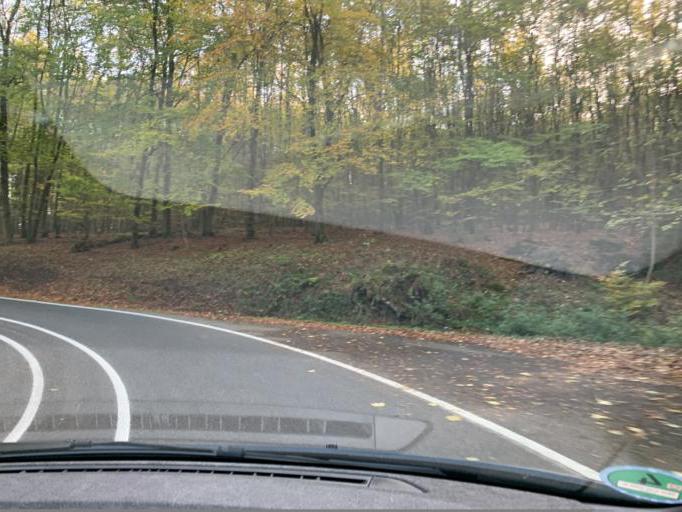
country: DE
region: North Rhine-Westphalia
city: Heimbach
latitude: 50.6087
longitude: 6.4803
